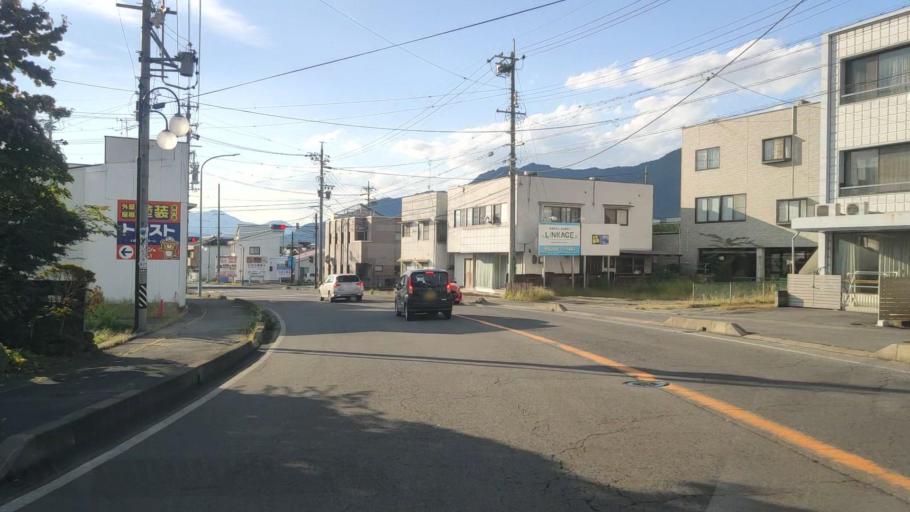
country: JP
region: Nagano
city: Ueda
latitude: 36.4044
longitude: 138.2619
